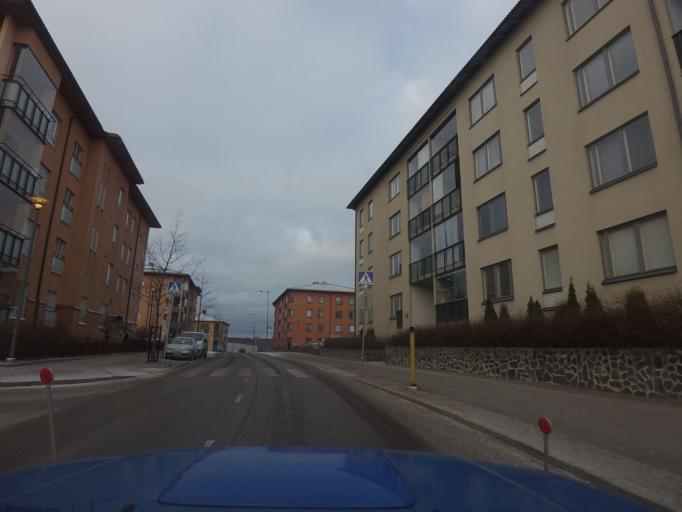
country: FI
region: Uusimaa
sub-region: Helsinki
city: Espoo
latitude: 60.2076
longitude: 24.6809
